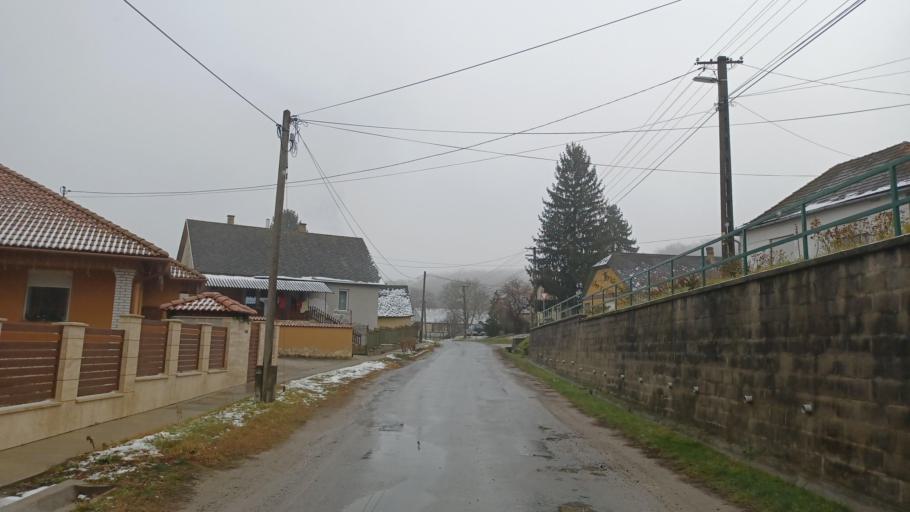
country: HU
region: Tolna
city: Pincehely
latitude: 46.6310
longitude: 18.4815
